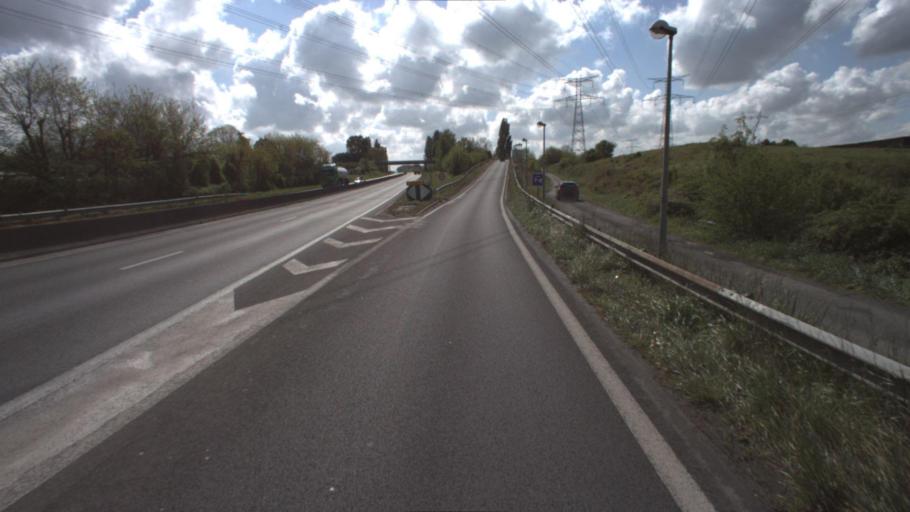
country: FR
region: Ile-de-France
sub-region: Departement de Seine-et-Marne
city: Ozoir-la-Ferriere
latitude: 48.7631
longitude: 2.6601
